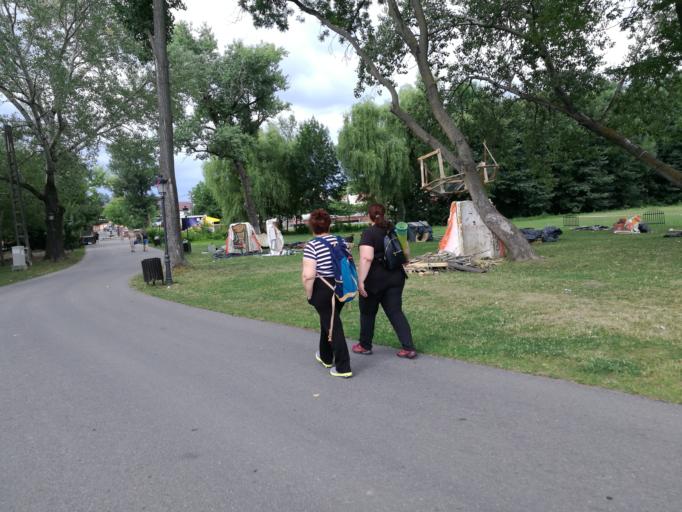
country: RO
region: Ilfov
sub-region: Comuna Mogosoaia
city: Mogosoaia
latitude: 44.5257
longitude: 25.9967
